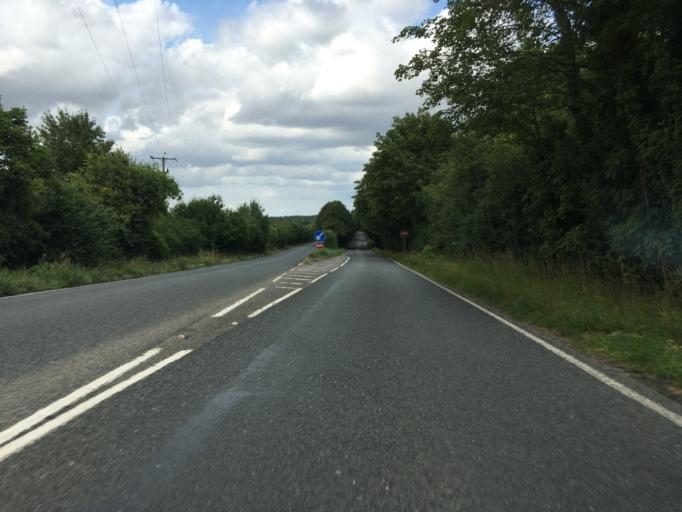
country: GB
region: England
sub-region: Hampshire
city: Kings Worthy
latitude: 51.1183
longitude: -1.2706
